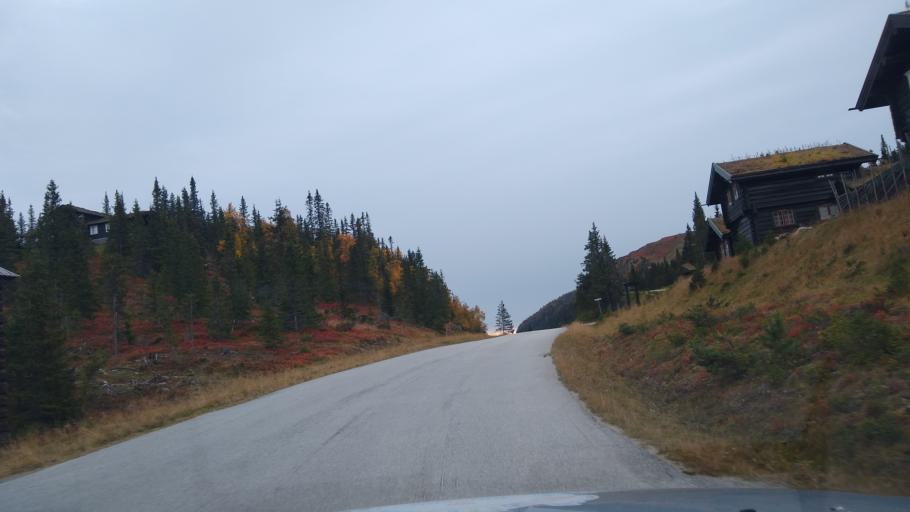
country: NO
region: Oppland
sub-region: Ringebu
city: Ringebu
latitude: 61.4792
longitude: 10.1249
